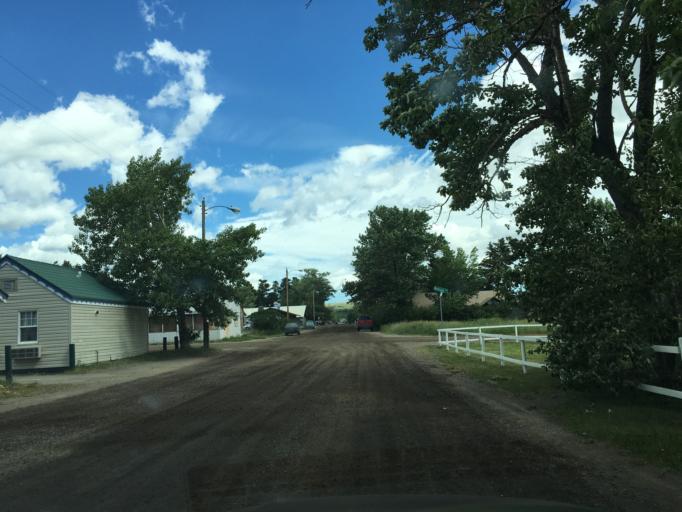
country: US
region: Montana
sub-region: Glacier County
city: South Browning
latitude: 48.4406
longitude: -113.2173
